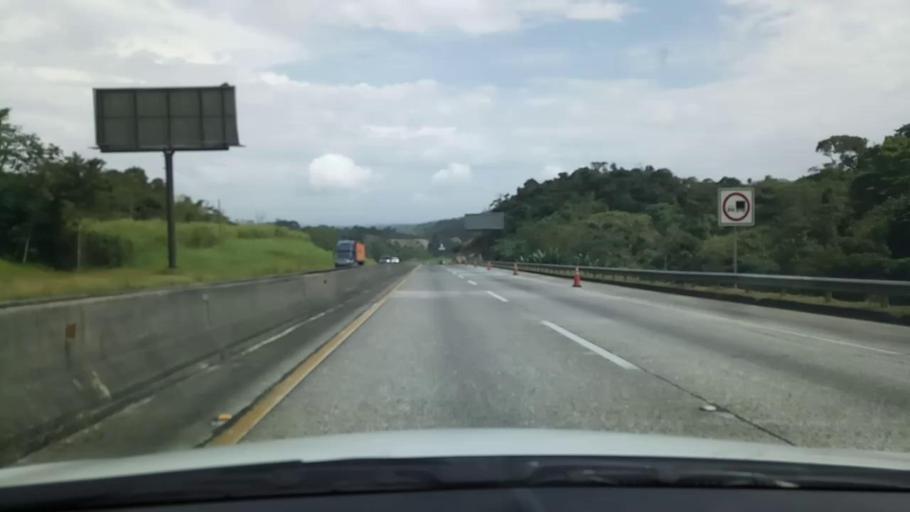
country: PA
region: Colon
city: Quebrada Bonita Adentro
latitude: 9.2821
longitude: -79.7319
